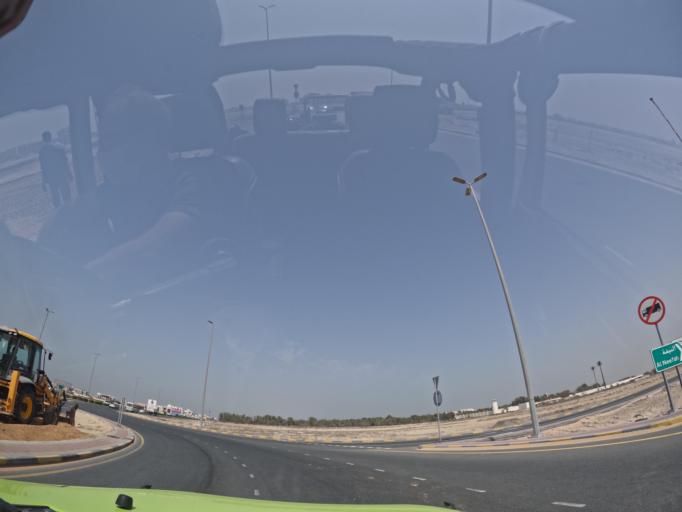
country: AE
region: Umm al Qaywayn
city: Umm al Qaywayn
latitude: 25.5231
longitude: 55.5580
